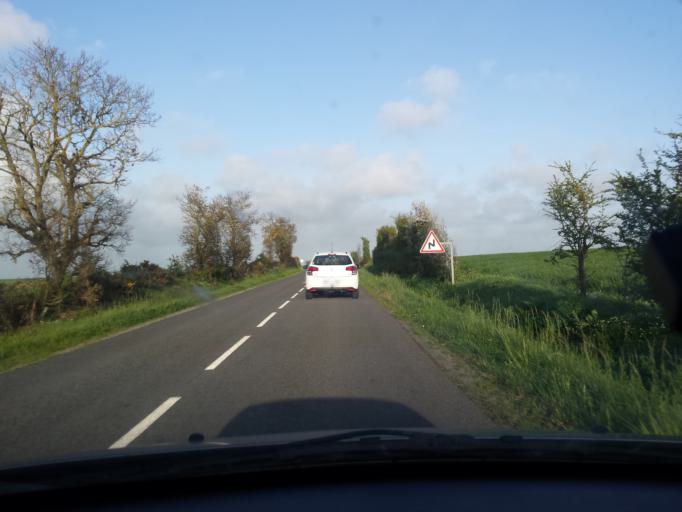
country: FR
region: Pays de la Loire
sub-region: Departement de la Vendee
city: Saint-Mathurin
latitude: 46.5694
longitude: -1.7446
